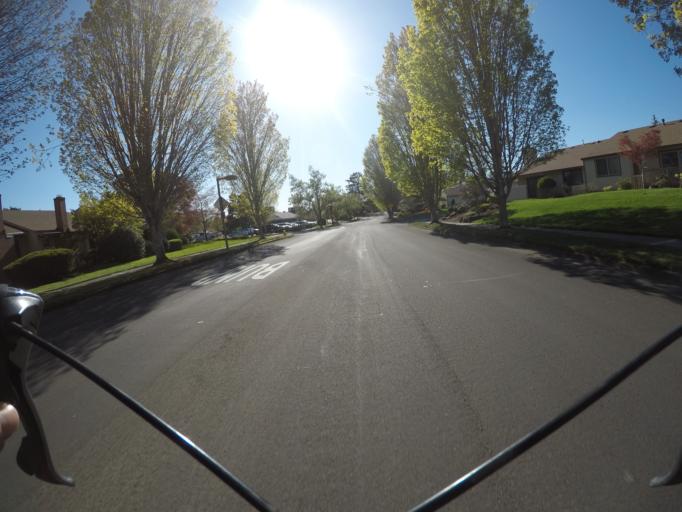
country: US
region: Oregon
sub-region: Washington County
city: King City
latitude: 45.4064
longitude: -122.7846
